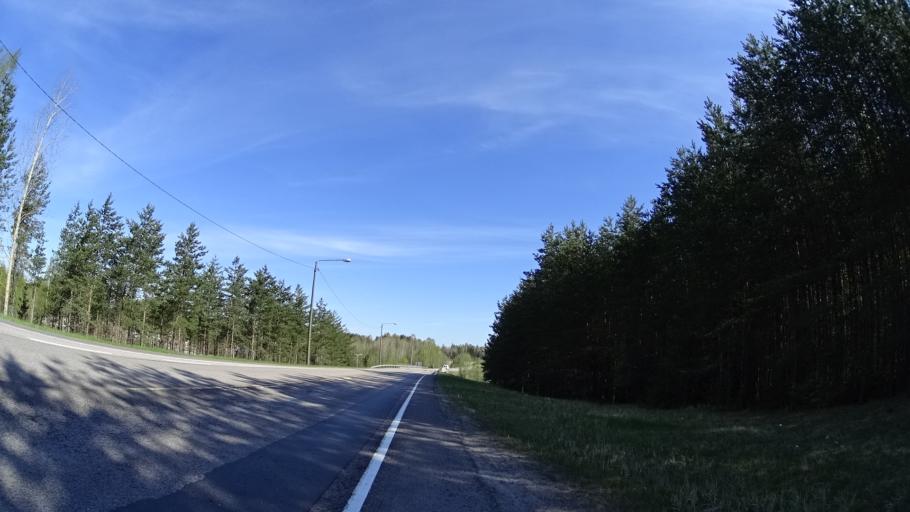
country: FI
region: Uusimaa
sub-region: Helsinki
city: Nurmijaervi
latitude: 60.4564
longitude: 24.8326
